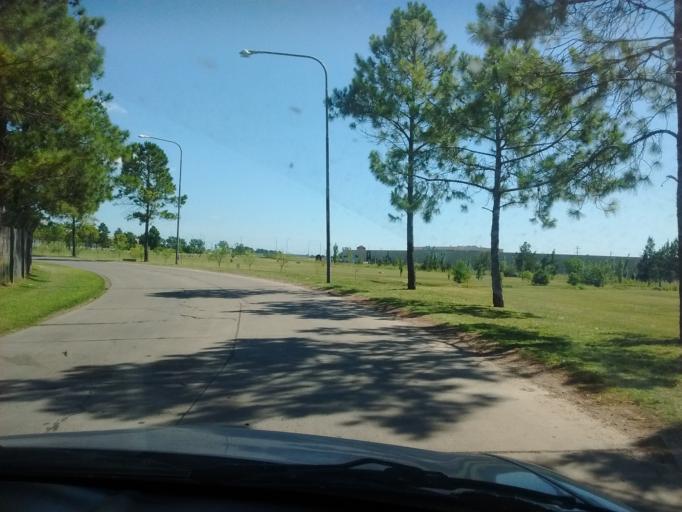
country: AR
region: Santa Fe
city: Funes
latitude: -32.9213
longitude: -60.7800
